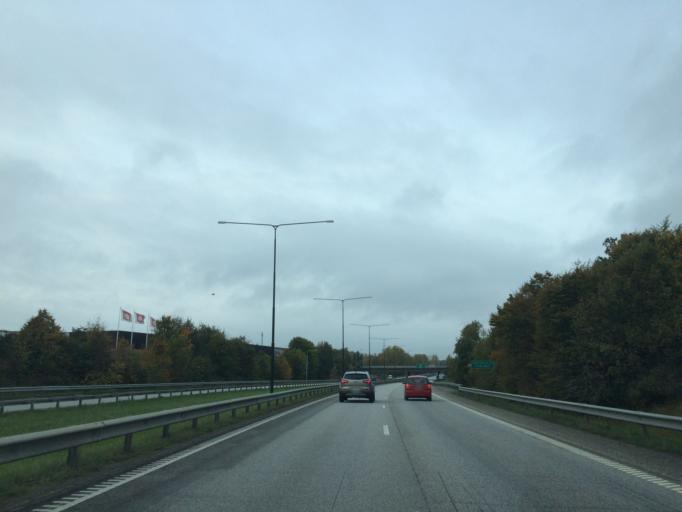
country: SE
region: Skane
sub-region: Malmo
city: Malmoe
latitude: 55.5658
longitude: 13.0365
